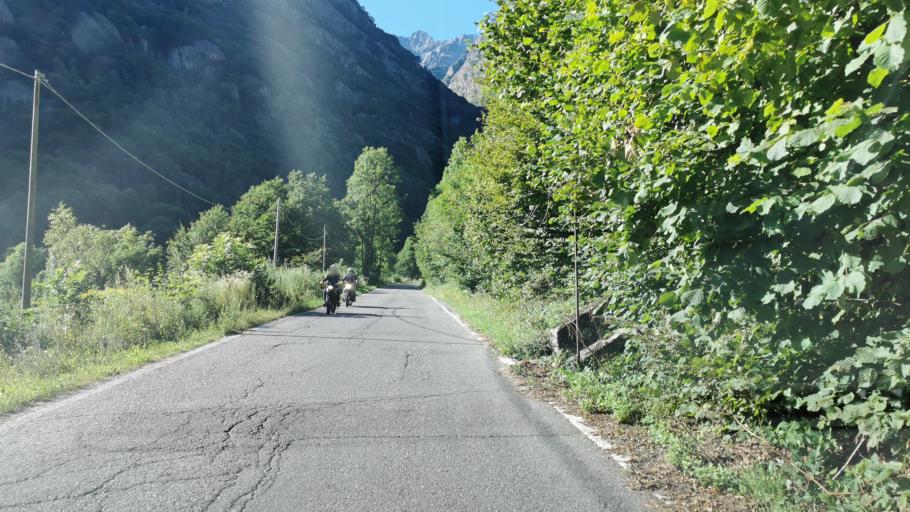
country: IT
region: Piedmont
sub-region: Provincia di Cuneo
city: Demonte
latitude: 44.2376
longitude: 7.3161
